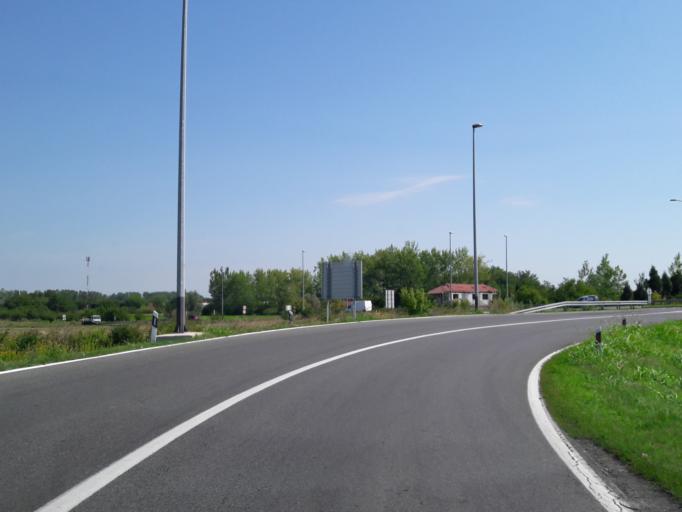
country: HR
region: Osjecko-Baranjska
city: Visnjevac
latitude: 45.5558
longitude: 18.6310
